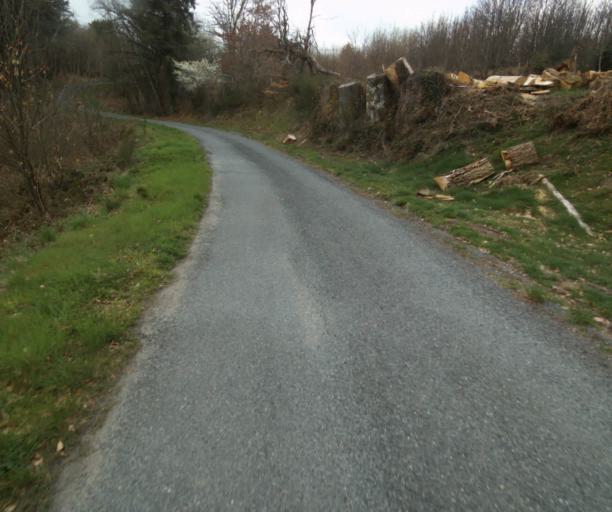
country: FR
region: Limousin
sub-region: Departement de la Correze
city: Correze
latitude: 45.2915
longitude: 1.9267
